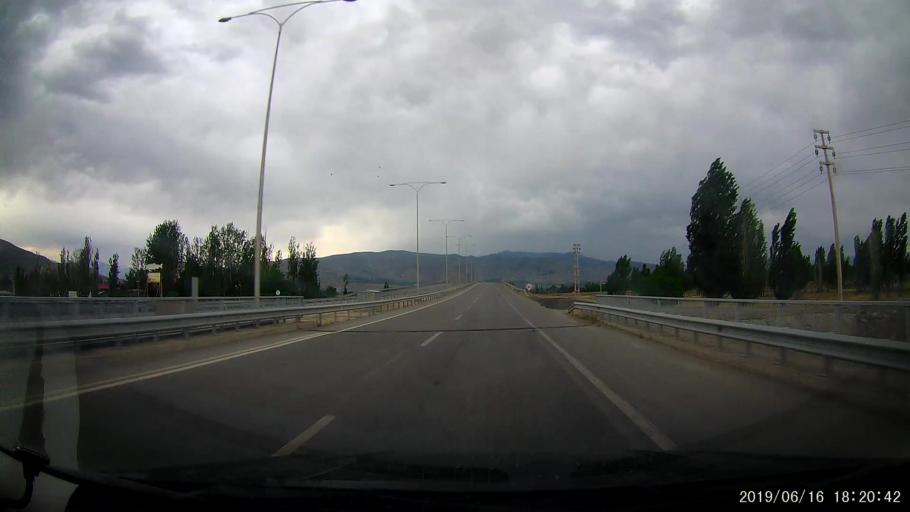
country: TR
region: Erzincan
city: Erzincan
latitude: 39.7203
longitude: 39.4626
